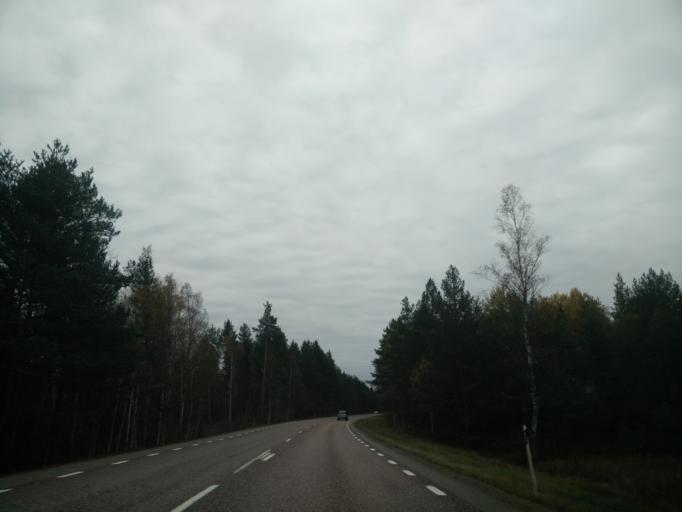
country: SE
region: Gaevleborg
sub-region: Gavle Kommun
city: Norrsundet
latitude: 60.8336
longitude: 17.2066
